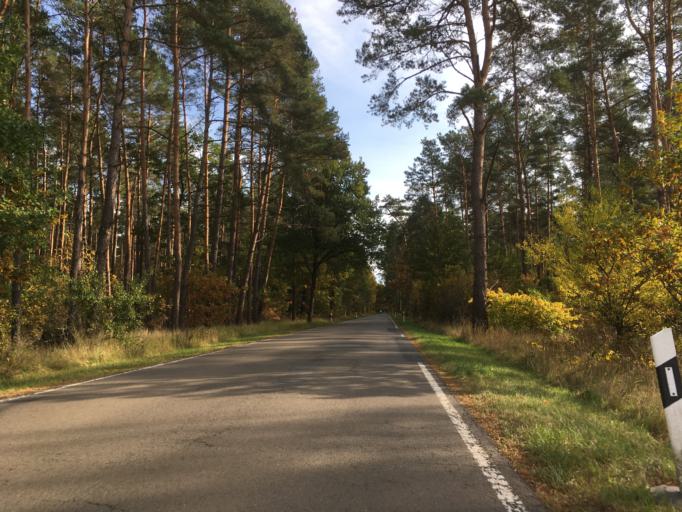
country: DE
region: Brandenburg
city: Templin
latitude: 53.0405
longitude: 13.4584
